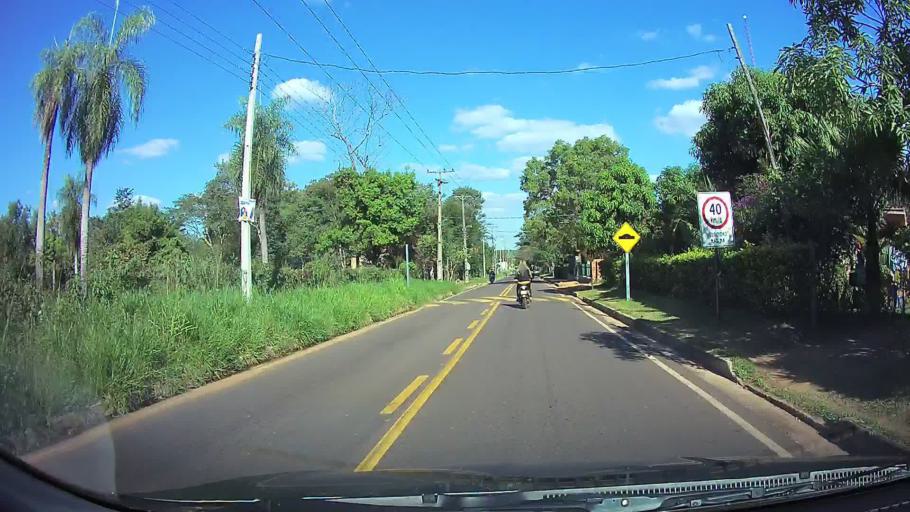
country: PY
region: Central
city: Limpio
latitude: -25.2082
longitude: -57.4795
